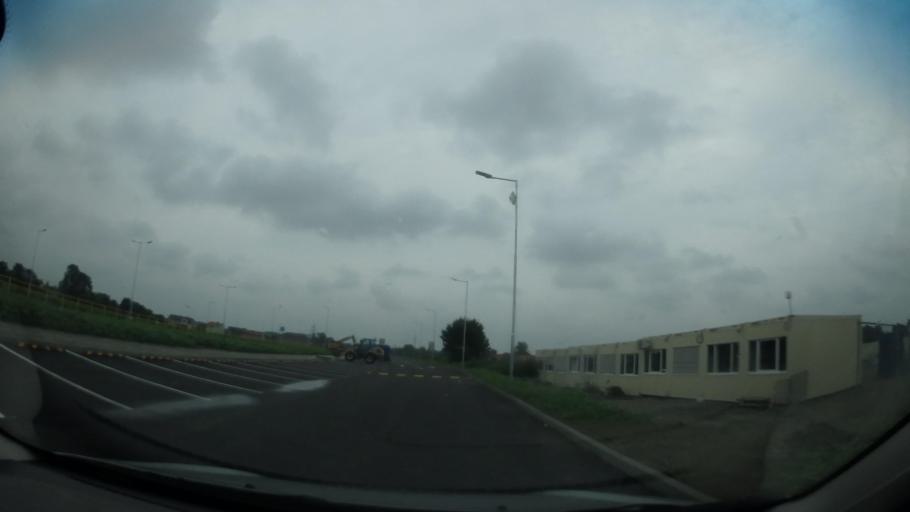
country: CZ
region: Olomoucky
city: Kojetin
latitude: 49.3390
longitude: 17.3093
